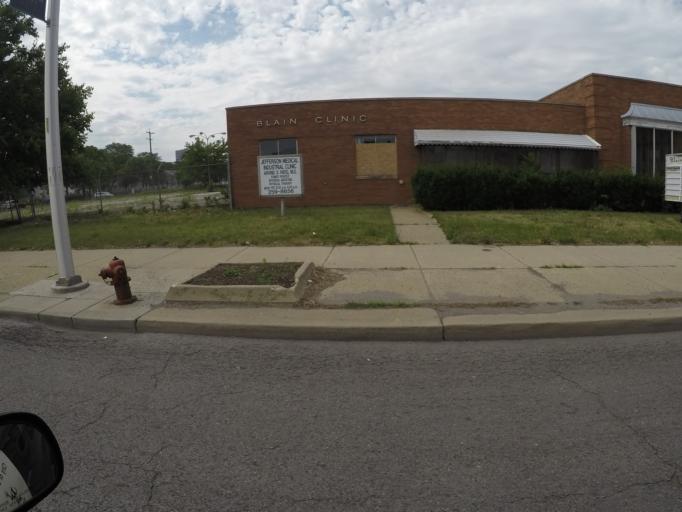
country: US
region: Michigan
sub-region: Wayne County
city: Detroit
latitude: 42.3371
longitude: -83.0254
